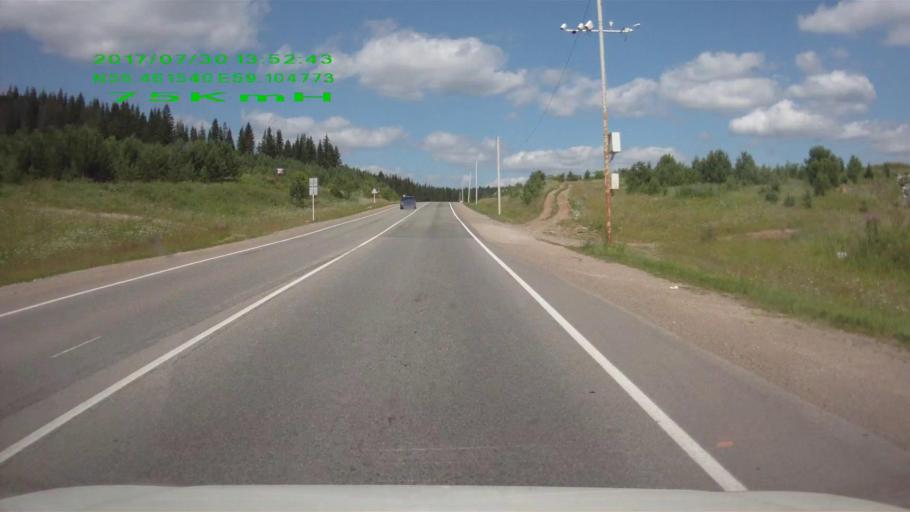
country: RU
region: Sverdlovsk
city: Mikhaylovsk
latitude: 56.4622
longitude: 59.1054
